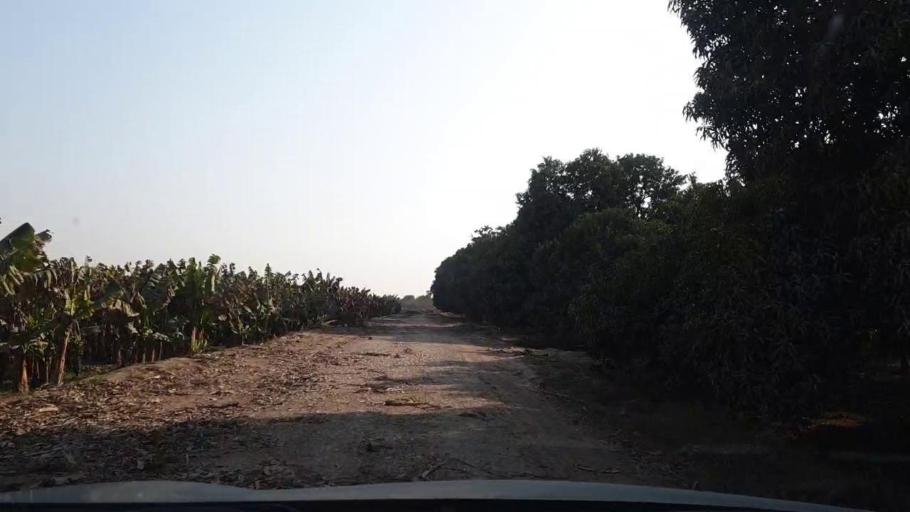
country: PK
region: Sindh
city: Tando Allahyar
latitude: 25.5705
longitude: 68.7642
